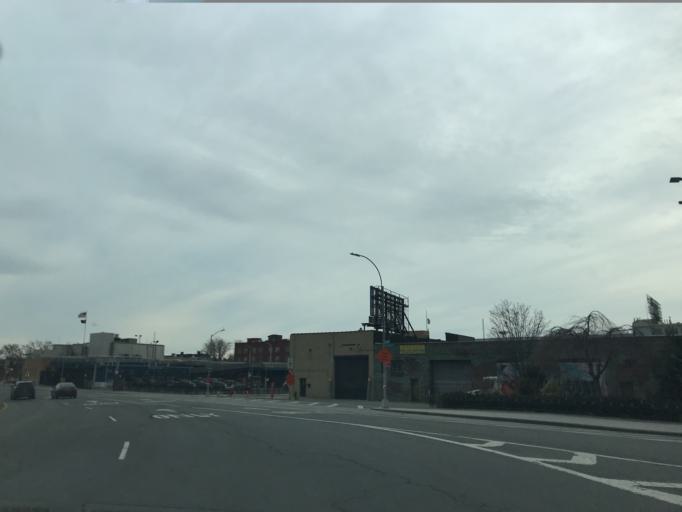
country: US
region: New York
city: New York City
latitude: 40.6817
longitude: -74.0058
